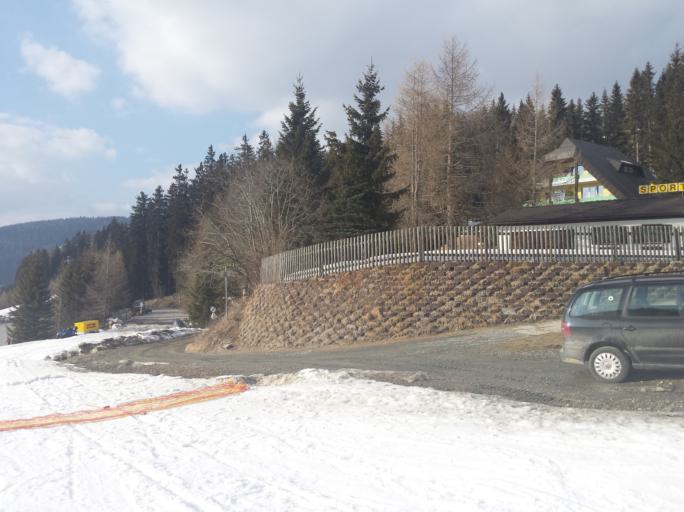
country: AT
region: Carinthia
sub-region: Politischer Bezirk Villach Land
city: Wernberg
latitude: 46.6810
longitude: 13.9043
